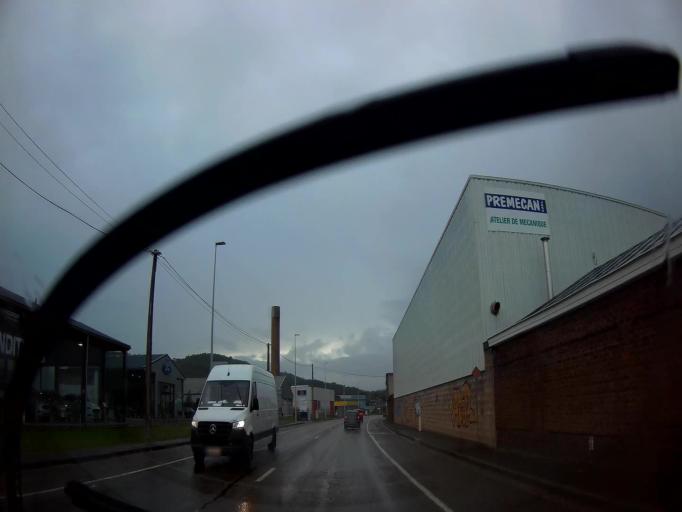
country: BE
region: Wallonia
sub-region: Province de Liege
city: Trooz
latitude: 50.5792
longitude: 5.6706
